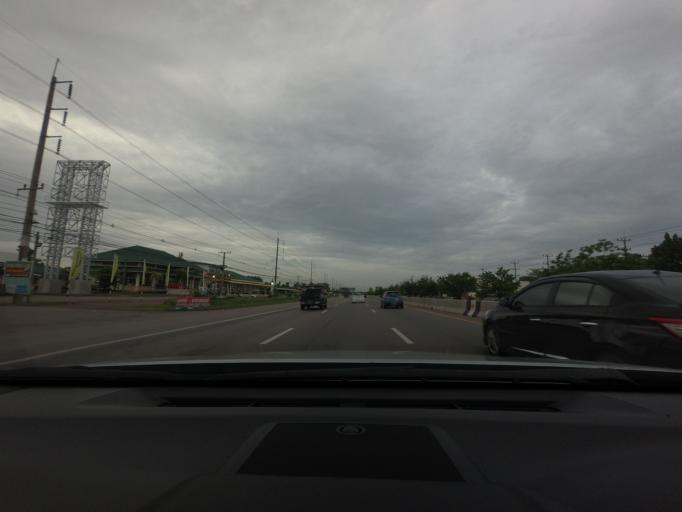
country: TH
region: Samut Songkhram
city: Amphawa
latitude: 13.3749
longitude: 99.9630
